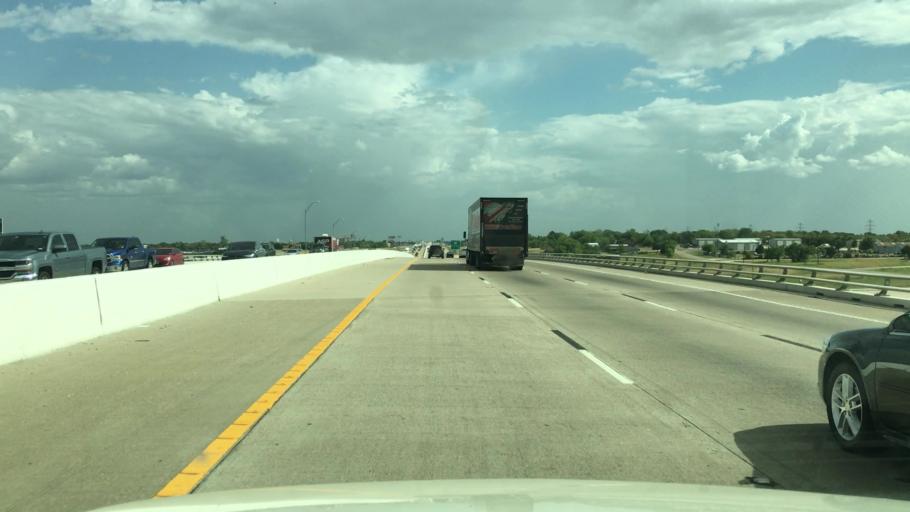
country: US
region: Texas
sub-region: McLennan County
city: Northcrest
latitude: 31.6885
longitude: -97.1001
